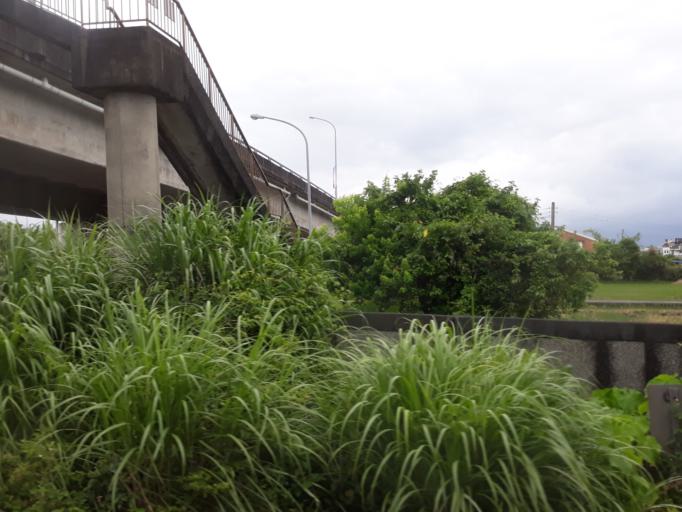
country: TW
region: Taiwan
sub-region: Yilan
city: Yilan
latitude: 24.6872
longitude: 121.7749
